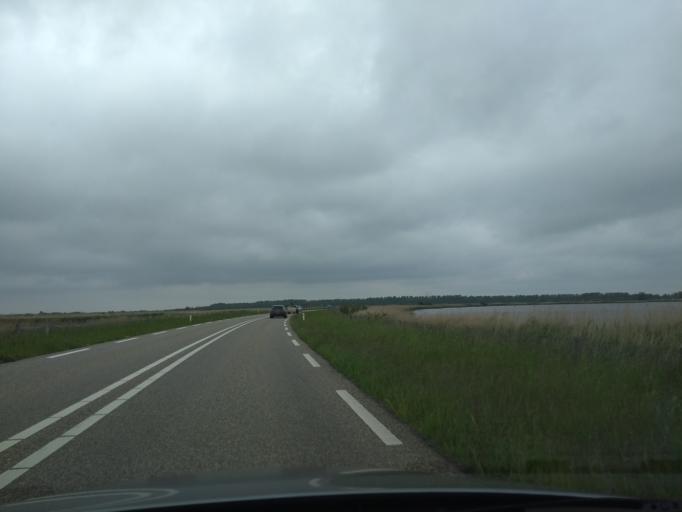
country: NL
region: Groningen
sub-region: Gemeente De Marne
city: Ulrum
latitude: 53.3670
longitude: 6.2423
